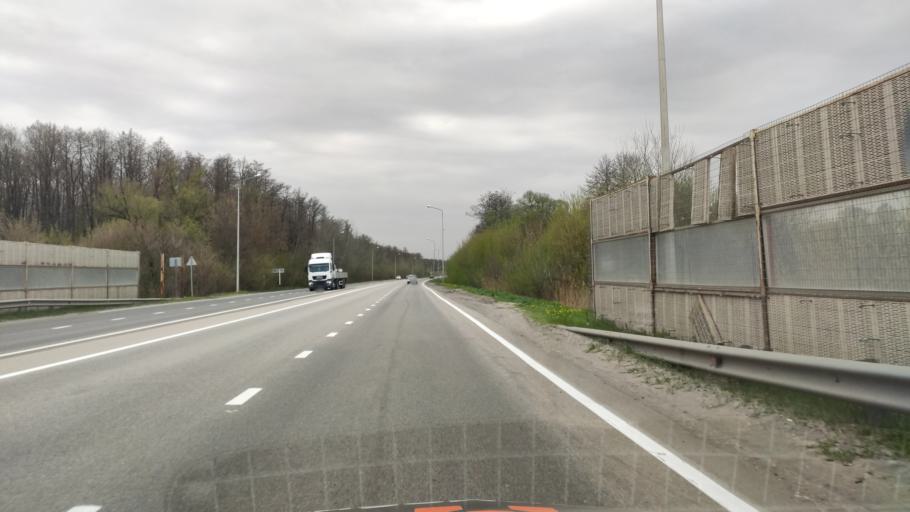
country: RU
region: Belgorod
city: Staryy Oskol
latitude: 51.3532
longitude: 37.8303
